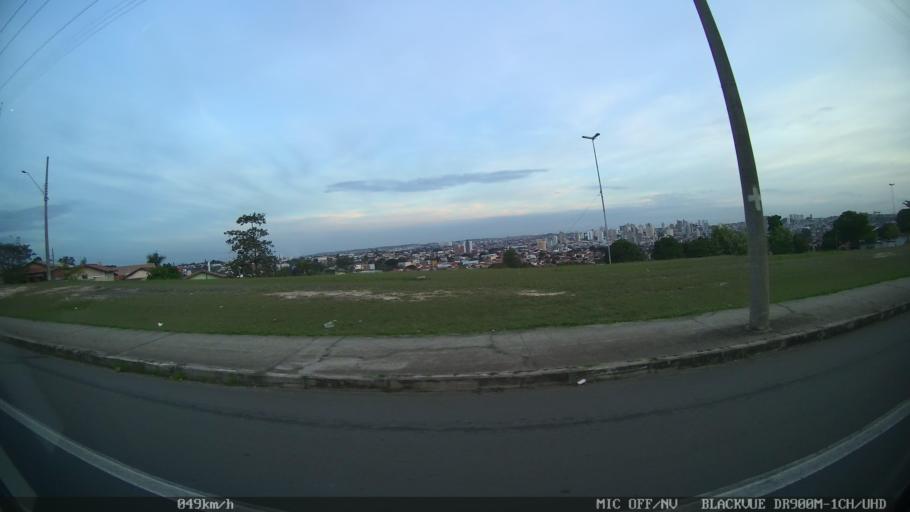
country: BR
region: Sao Paulo
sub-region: Limeira
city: Limeira
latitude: -22.5460
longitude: -47.3925
